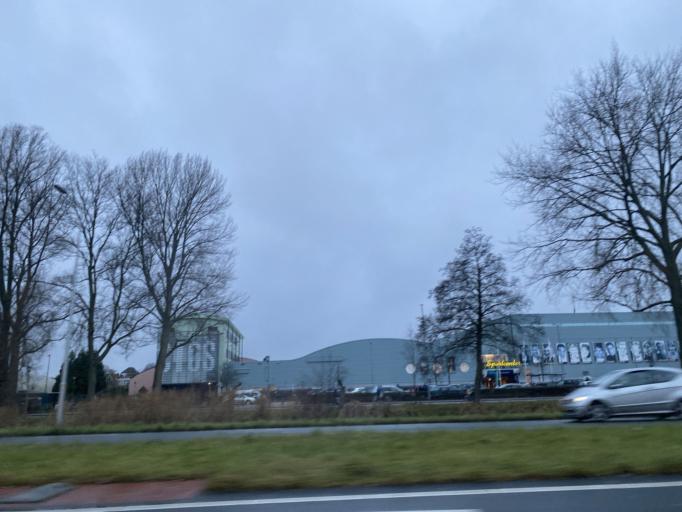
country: NL
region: North Holland
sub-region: Gemeente Bloemendaal
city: Bloemendaal
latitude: 52.3998
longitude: 4.6285
